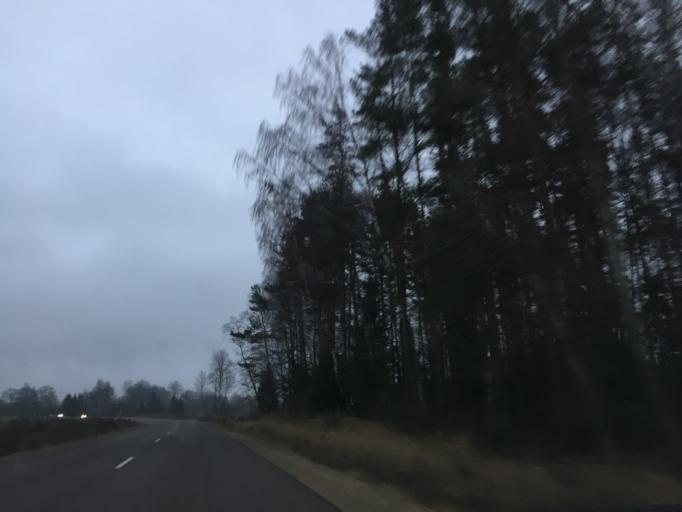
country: LV
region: Koceni
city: Koceni
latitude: 57.5501
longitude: 25.3696
